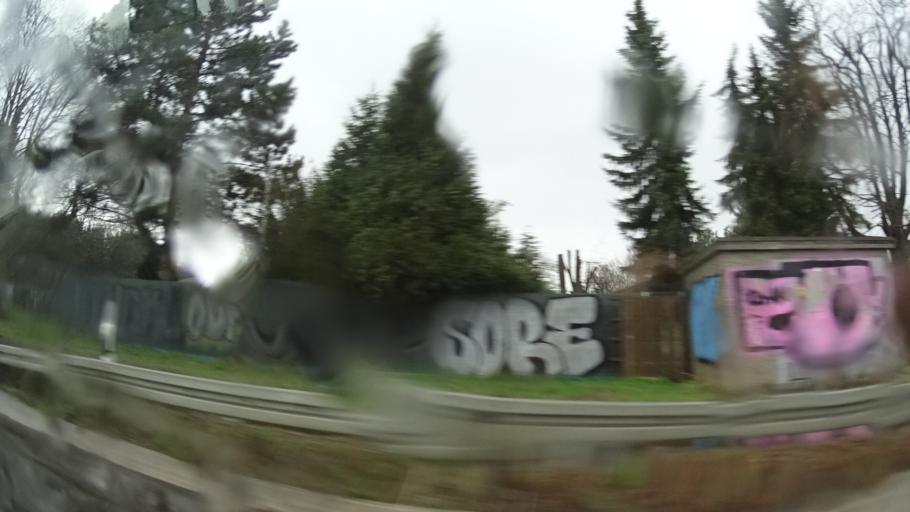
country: DE
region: Hesse
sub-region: Regierungsbezirk Darmstadt
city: Bad Vilbel
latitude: 50.1535
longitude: 8.7152
